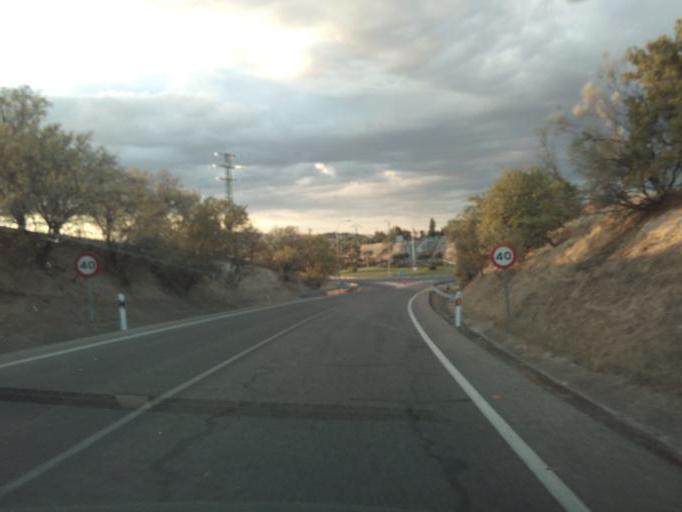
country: ES
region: Madrid
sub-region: Provincia de Madrid
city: Algete
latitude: 40.5948
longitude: -3.5085
